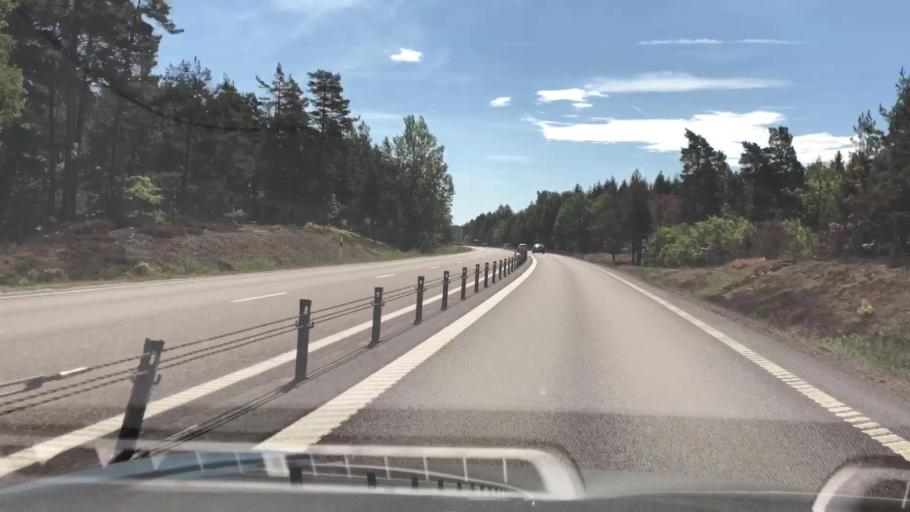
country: SE
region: Kalmar
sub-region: Oskarshamns Kommun
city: Paskallavik
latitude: 57.1599
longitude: 16.4481
